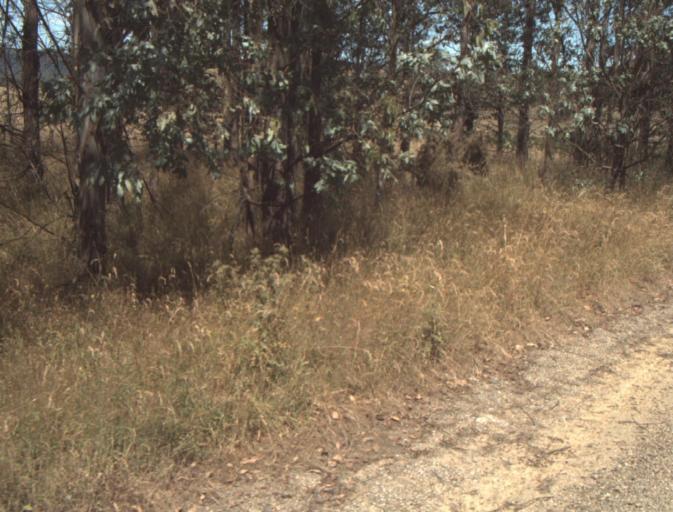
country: AU
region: Tasmania
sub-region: Dorset
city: Scottsdale
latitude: -41.3290
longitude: 147.4425
